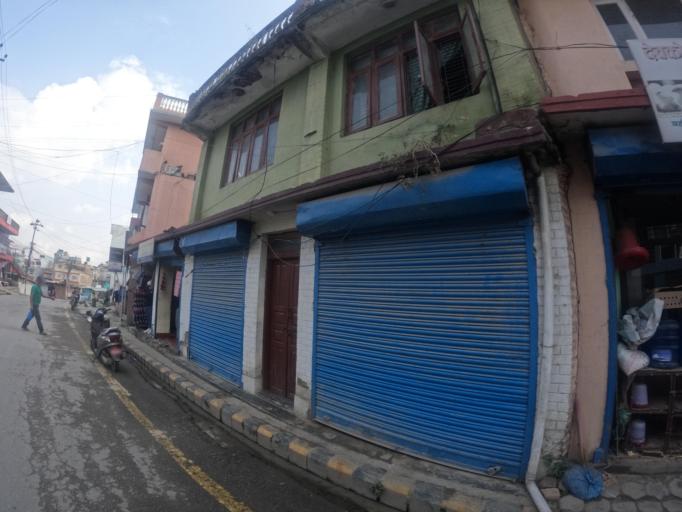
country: NP
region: Central Region
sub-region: Bagmati Zone
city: Patan
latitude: 27.6663
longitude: 85.3662
